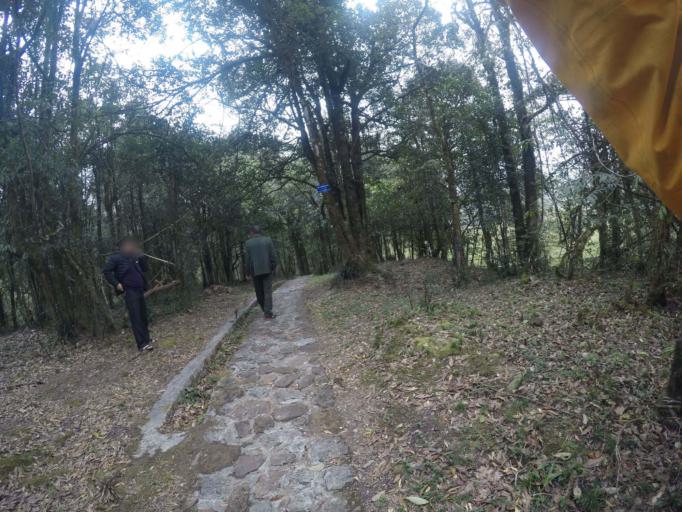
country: VN
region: Lao Cai
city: Sa Pa
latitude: 22.3505
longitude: 103.7718
